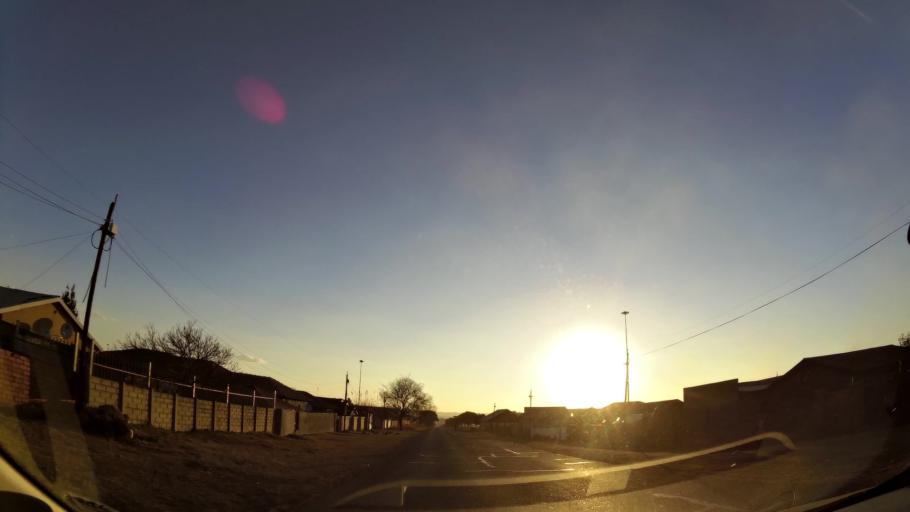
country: ZA
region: Mpumalanga
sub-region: Nkangala District Municipality
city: Witbank
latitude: -25.8838
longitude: 29.1865
